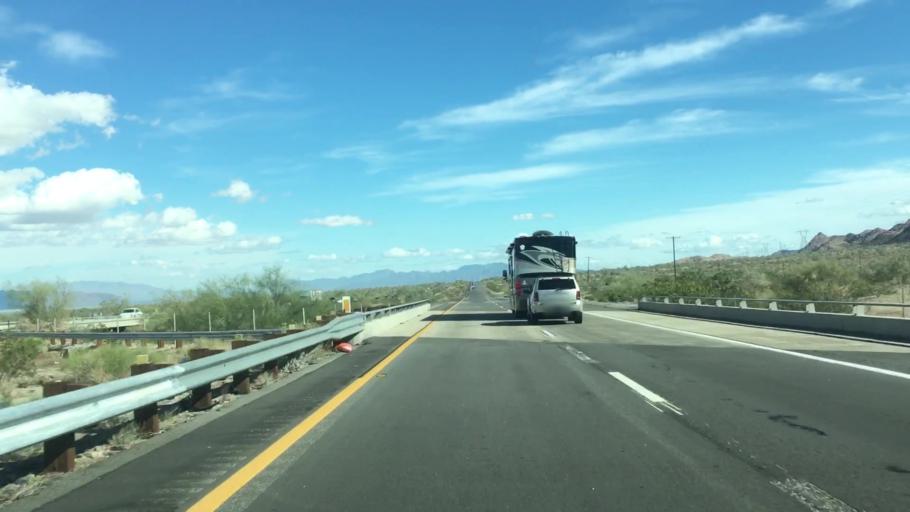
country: US
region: California
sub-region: Imperial County
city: Niland
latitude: 33.6912
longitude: -115.5025
